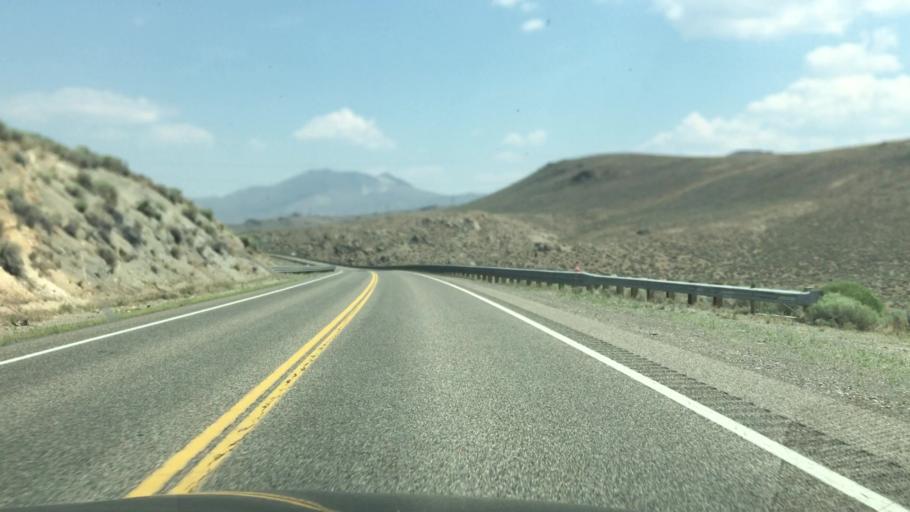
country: US
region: Nevada
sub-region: Elko County
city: Jackpot
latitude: 41.7420
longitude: -114.7759
